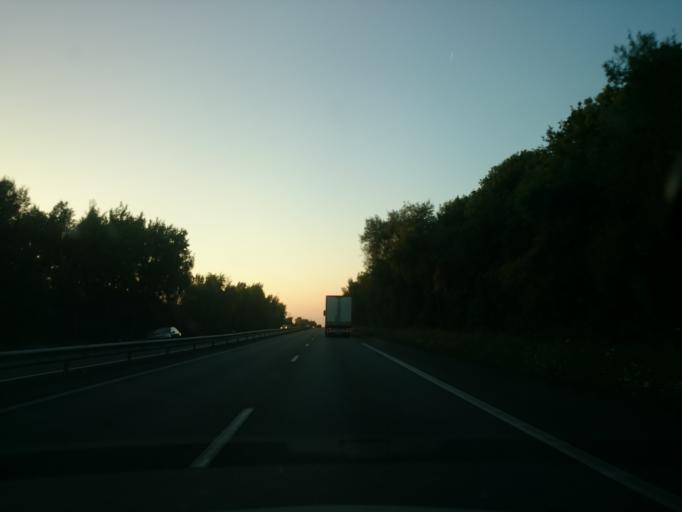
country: FR
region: Pays de la Loire
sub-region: Departement de la Loire-Atlantique
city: Derval
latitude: 47.6688
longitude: -1.6860
